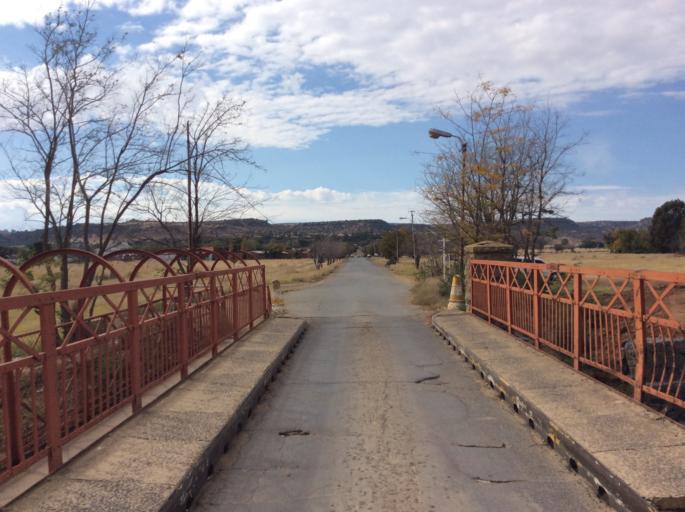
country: LS
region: Mafeteng
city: Mafeteng
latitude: -29.7313
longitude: 27.0335
